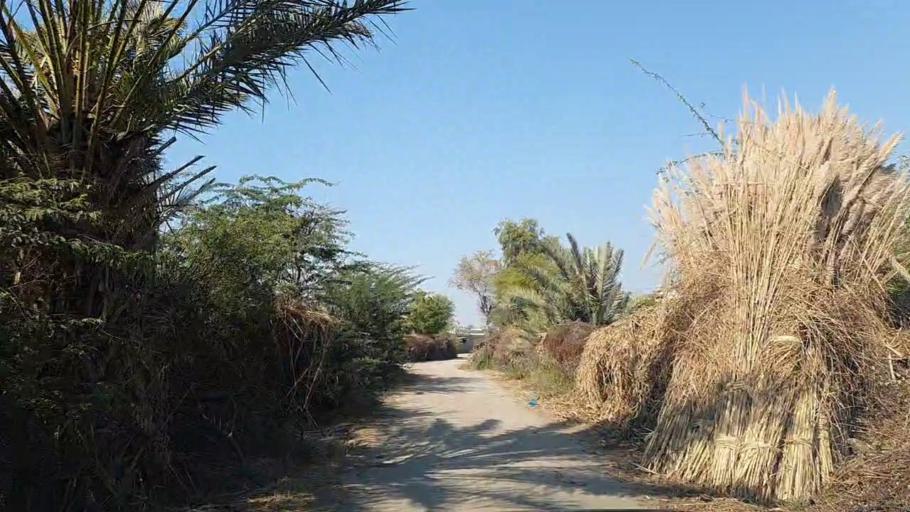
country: PK
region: Sindh
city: Nawabshah
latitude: 26.3472
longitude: 68.3815
